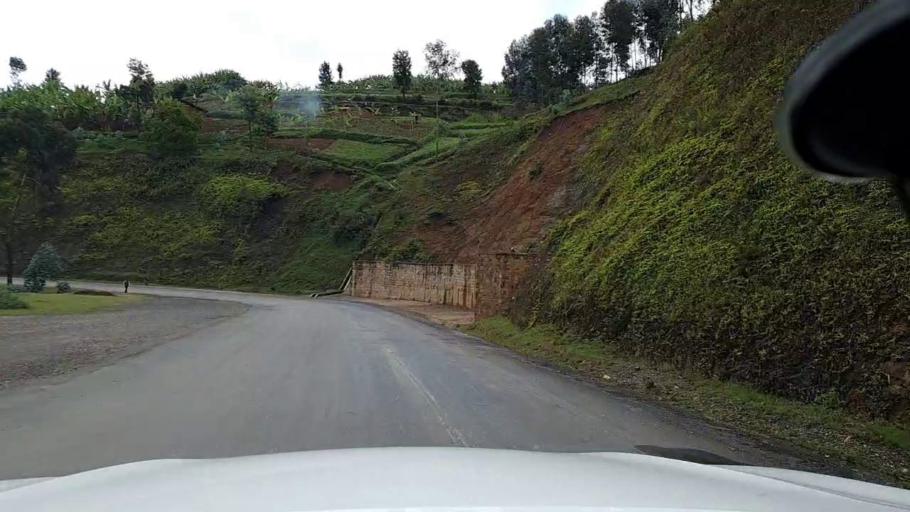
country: RW
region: Southern Province
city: Gitarama
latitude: -2.0659
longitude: 29.5549
